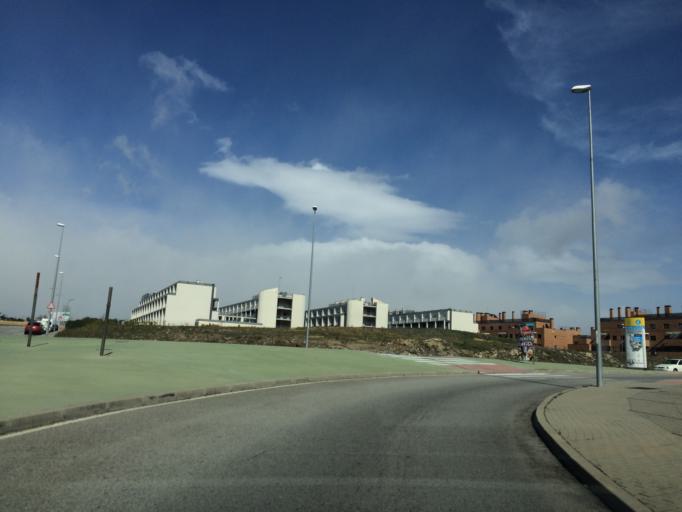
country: ES
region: Madrid
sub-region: Provincia de Madrid
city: Colmenar Viejo
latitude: 40.6598
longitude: -3.7577
